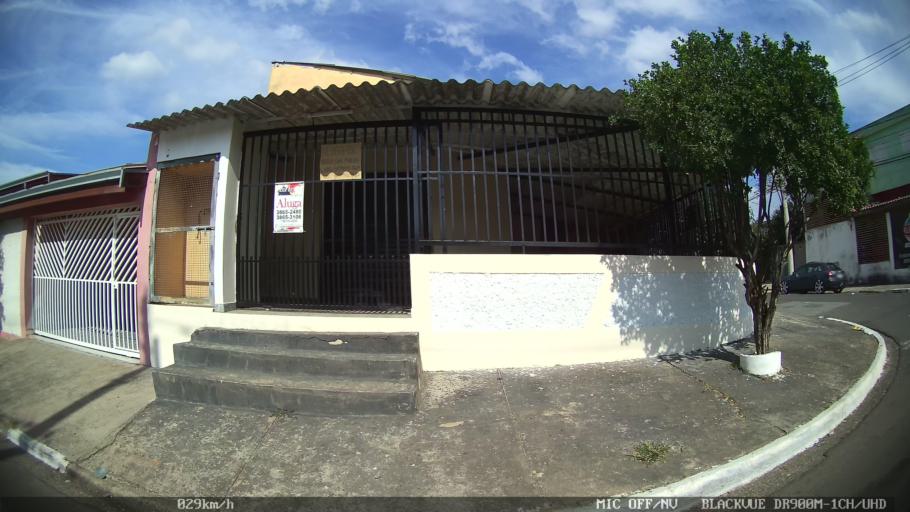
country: BR
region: Sao Paulo
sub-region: Hortolandia
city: Hortolandia
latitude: -22.9040
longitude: -47.2379
